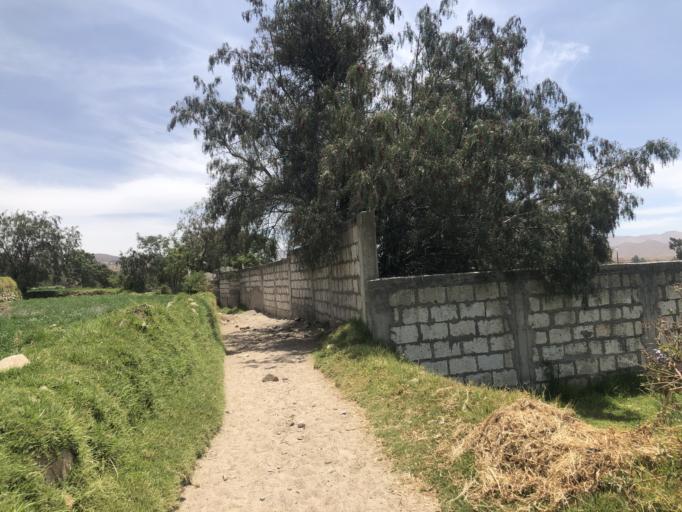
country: PE
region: Arequipa
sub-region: Provincia de Arequipa
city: Quequena
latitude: -16.5546
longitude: -71.4528
